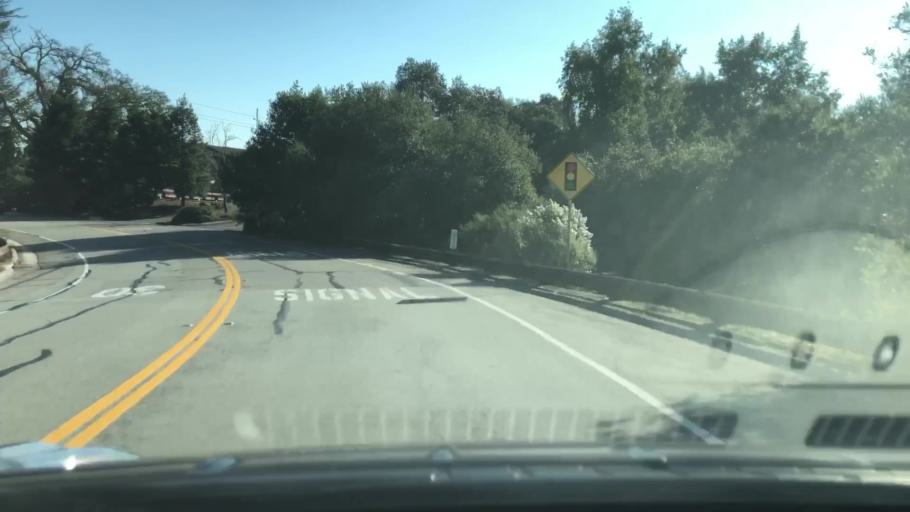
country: US
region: California
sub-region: Santa Clara County
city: Loyola
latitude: 37.3315
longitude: -122.0710
